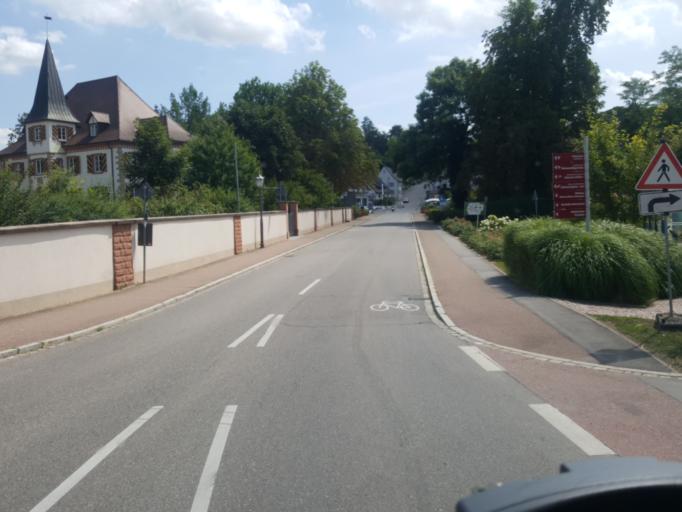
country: DE
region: Baden-Wuerttemberg
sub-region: Freiburg Region
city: Schliengen
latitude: 47.7553
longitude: 7.5776
